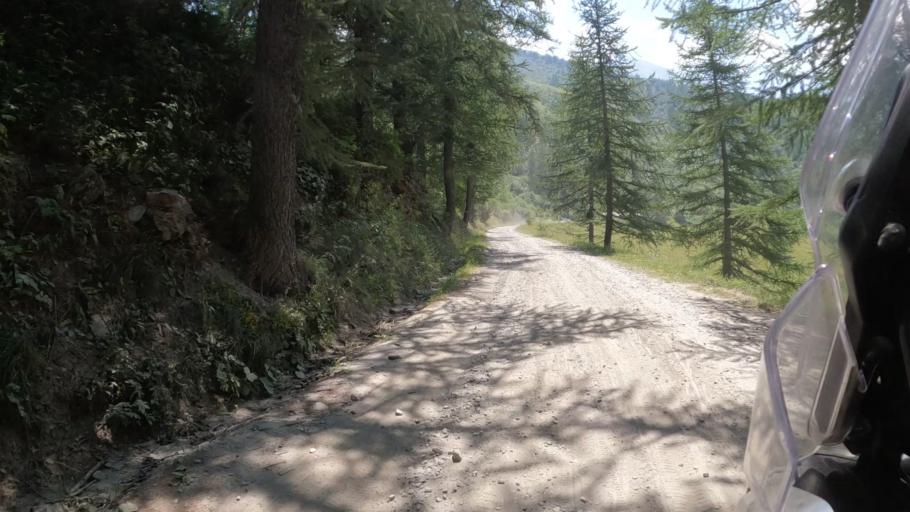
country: IT
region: Piedmont
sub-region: Provincia di Torino
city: Meana di Susa
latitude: 45.0892
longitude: 7.0622
